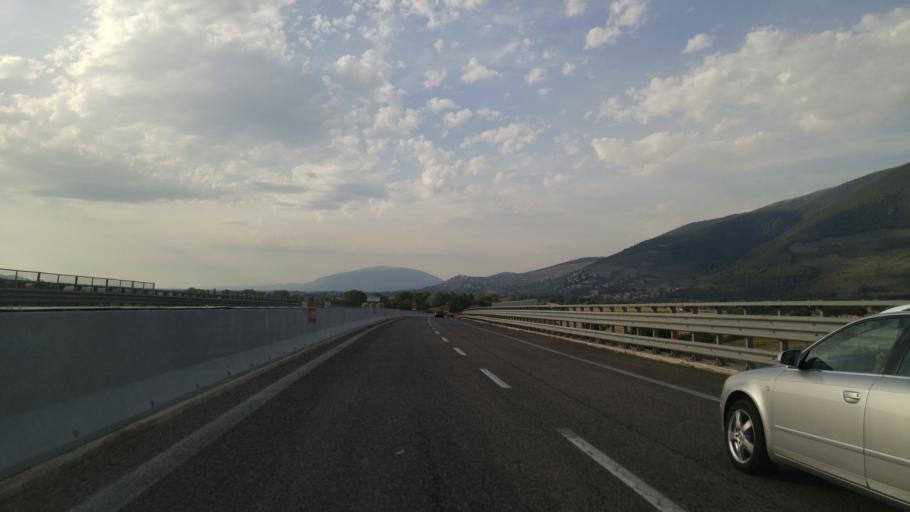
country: IT
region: Umbria
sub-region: Provincia di Perugia
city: San Giacomo
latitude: 42.8107
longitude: 12.7580
